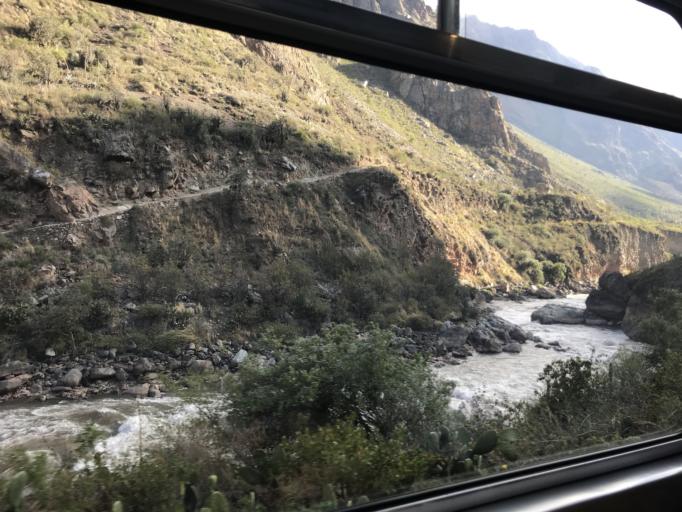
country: PE
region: Cusco
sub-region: Provincia de Urubamba
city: Ollantaytambo
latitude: -13.2156
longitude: -72.3844
